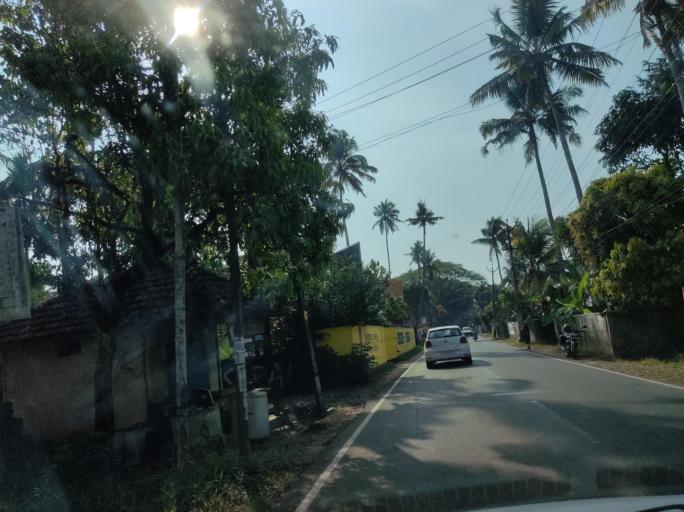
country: IN
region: Kerala
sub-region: Alappuzha
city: Shertallai
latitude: 9.6832
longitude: 76.3567
